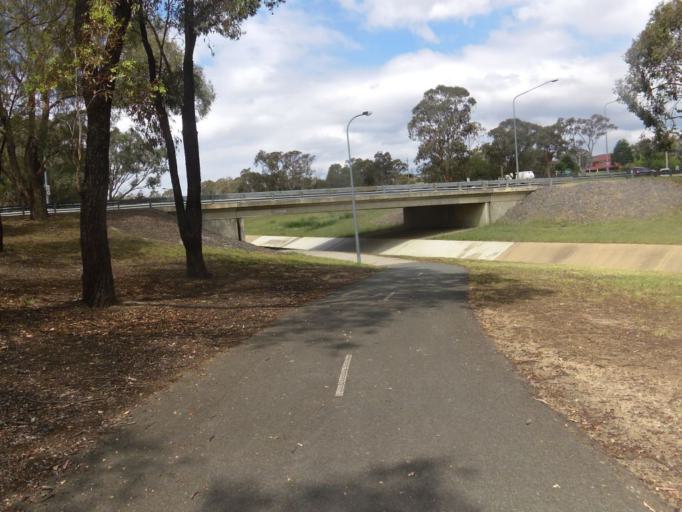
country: AU
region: Australian Capital Territory
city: Macarthur
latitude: -35.4158
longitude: 149.1136
